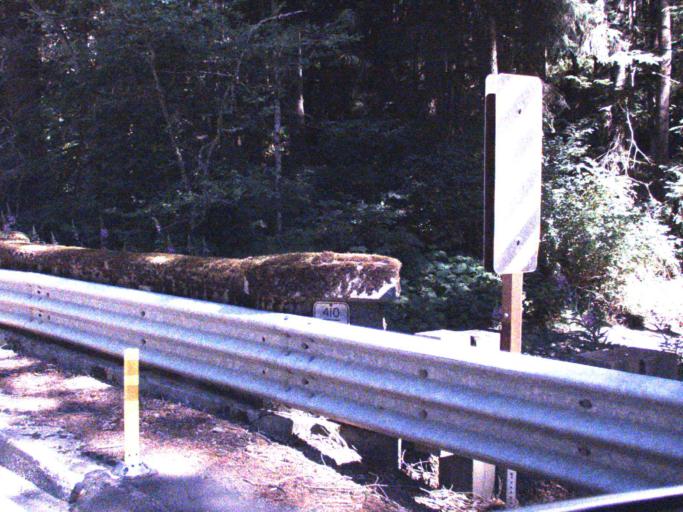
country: US
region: Washington
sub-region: King County
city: Enumclaw
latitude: 47.1634
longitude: -121.7402
